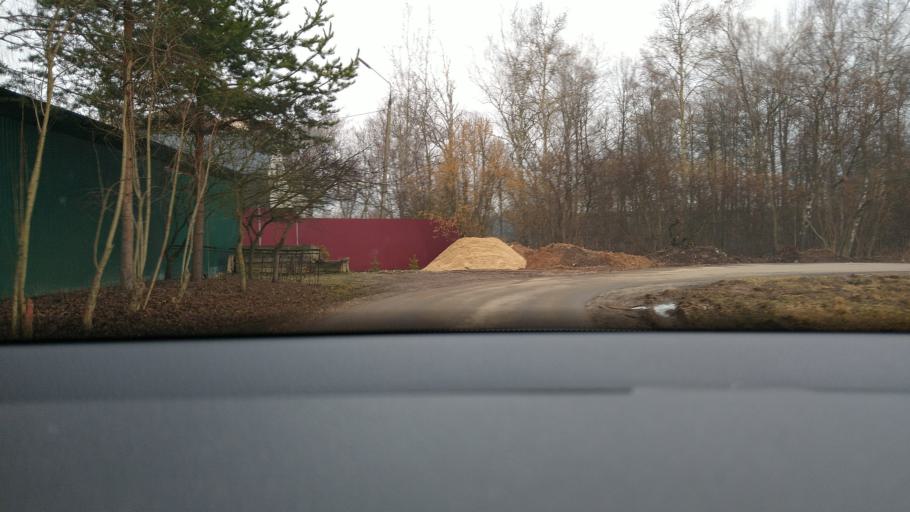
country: RU
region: Moskovskaya
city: Vatutinki
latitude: 55.5191
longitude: 37.3399
